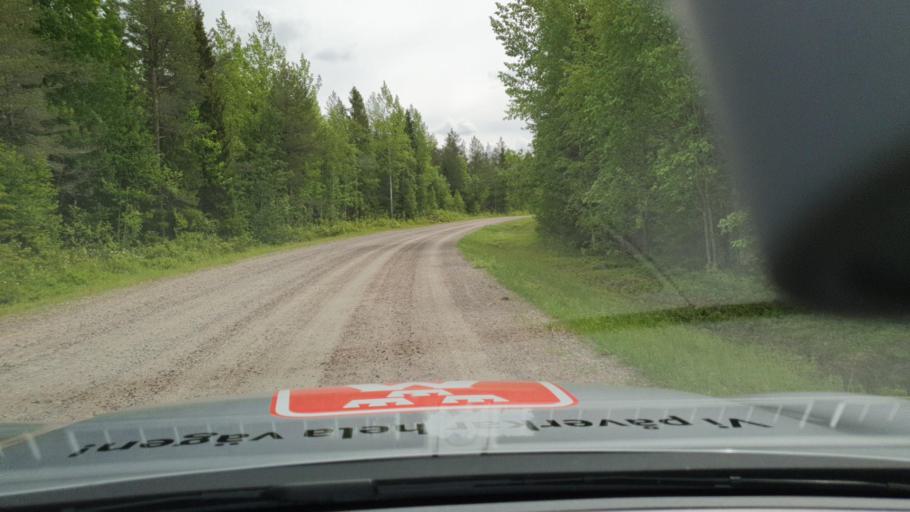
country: FI
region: Lapland
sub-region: Torniolaakso
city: Ylitornio
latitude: 65.9629
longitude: 23.7251
